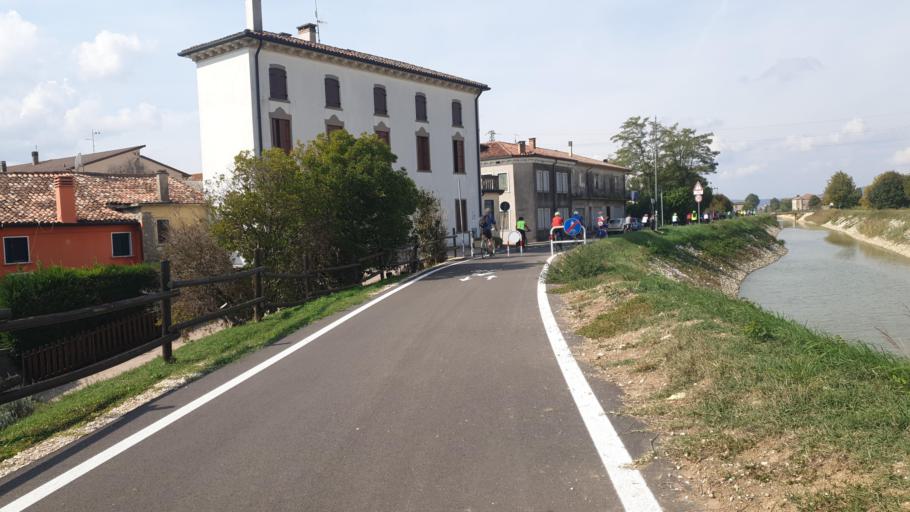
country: IT
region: Veneto
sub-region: Provincia di Vicenza
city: Agugliaro
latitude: 45.3253
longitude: 11.5883
